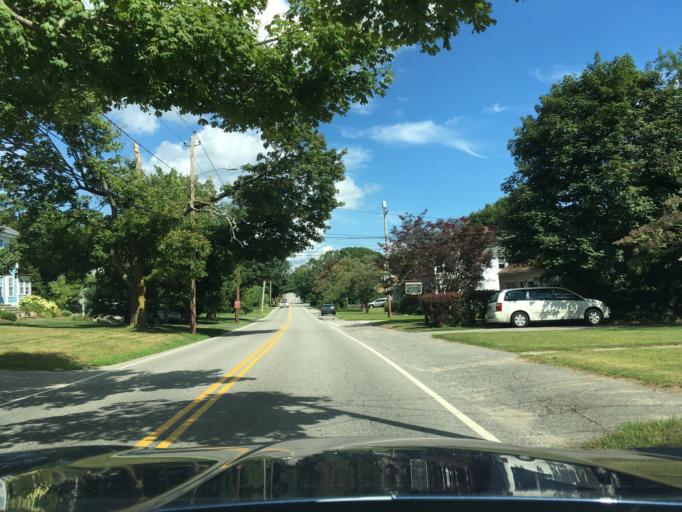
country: US
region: Rhode Island
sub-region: Bristol County
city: Barrington
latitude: 41.7388
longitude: -71.3281
